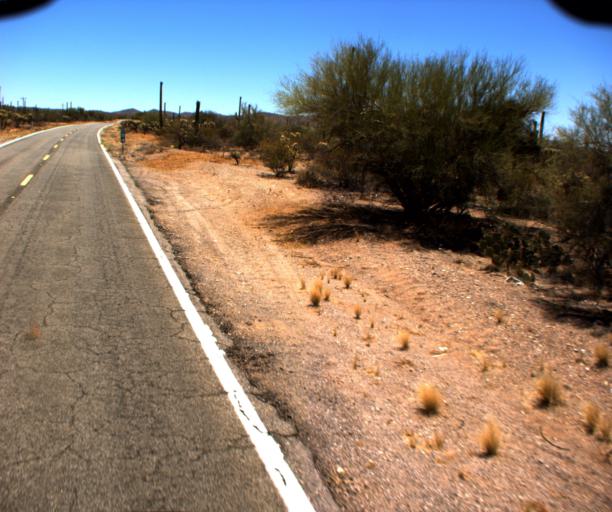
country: US
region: Arizona
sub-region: Pima County
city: Sells
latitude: 32.1770
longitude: -112.2454
